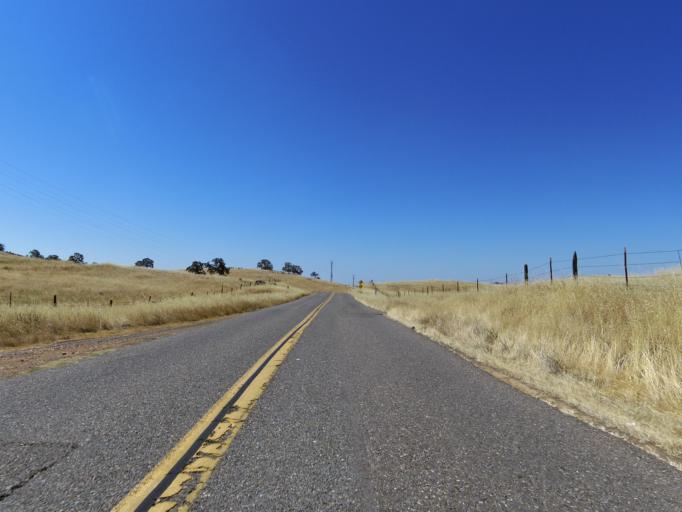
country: US
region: California
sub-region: Merced County
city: Planada
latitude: 37.5522
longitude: -120.3254
